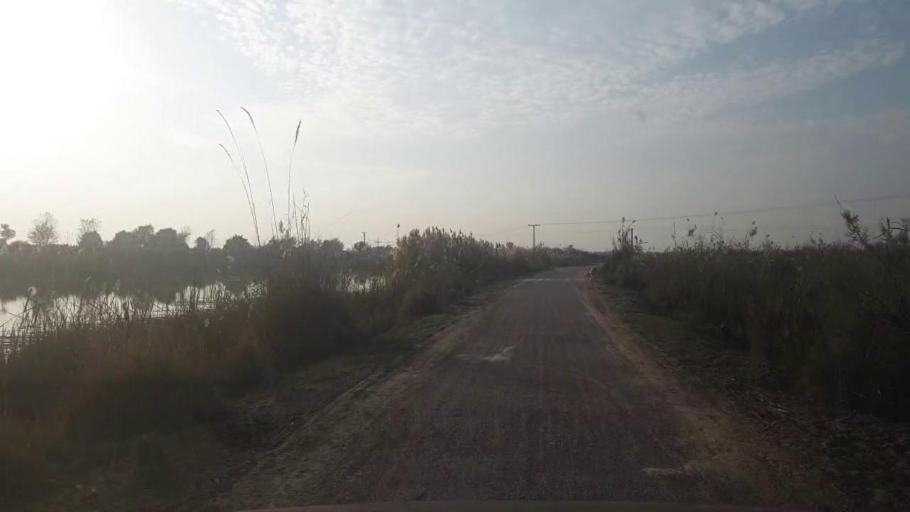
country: PK
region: Sindh
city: Sakrand
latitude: 26.0993
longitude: 68.4003
